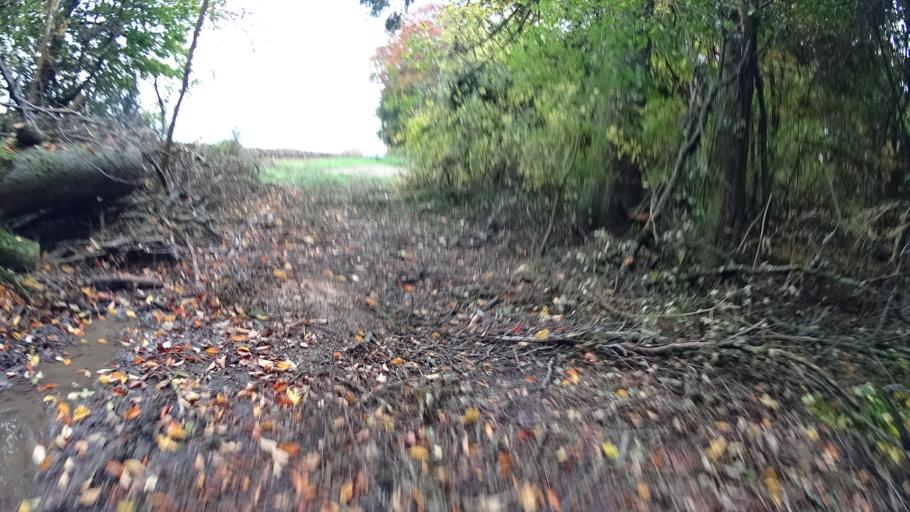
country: DE
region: Bavaria
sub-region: Upper Bavaria
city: Eichstaett
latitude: 48.8703
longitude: 11.2327
